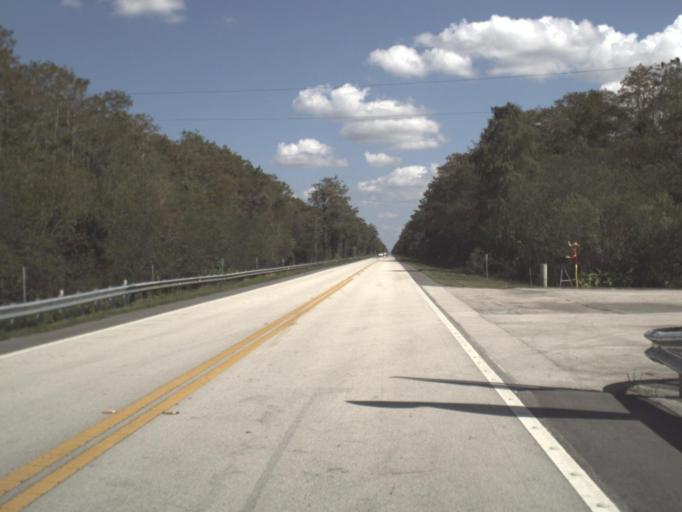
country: US
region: Florida
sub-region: Miami-Dade County
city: Kendall West
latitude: 25.8555
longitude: -81.0202
